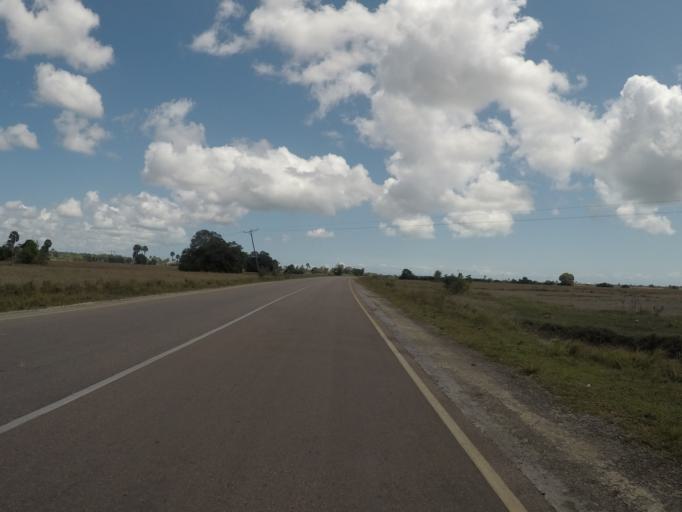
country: TZ
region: Zanzibar Central/South
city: Koani
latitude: -6.1970
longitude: 39.3701
